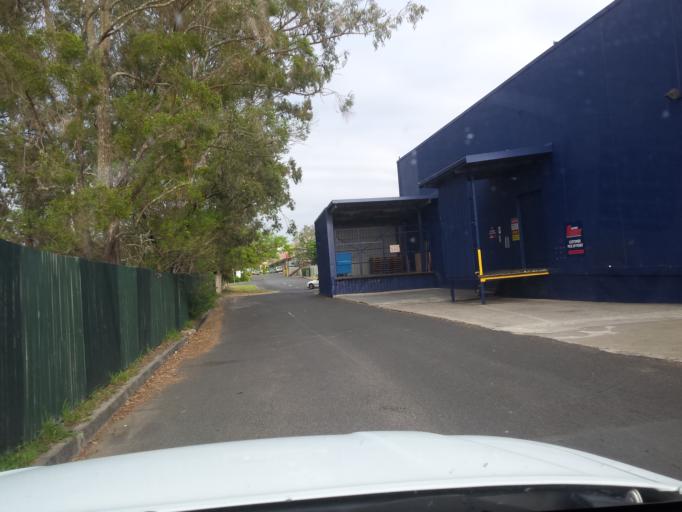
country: AU
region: Queensland
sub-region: Logan
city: Logan City
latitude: -27.6441
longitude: 153.1157
